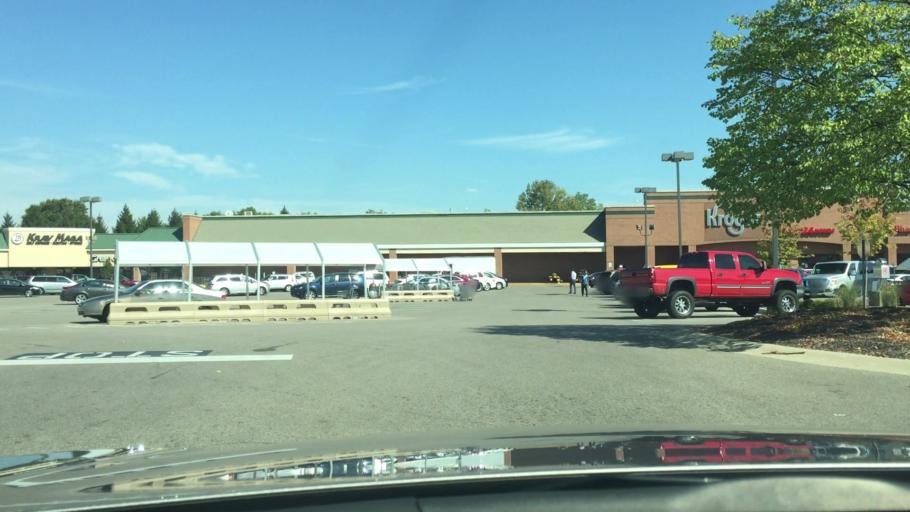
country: US
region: Indiana
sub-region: Hamilton County
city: Fishers
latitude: 39.9574
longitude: -86.0419
